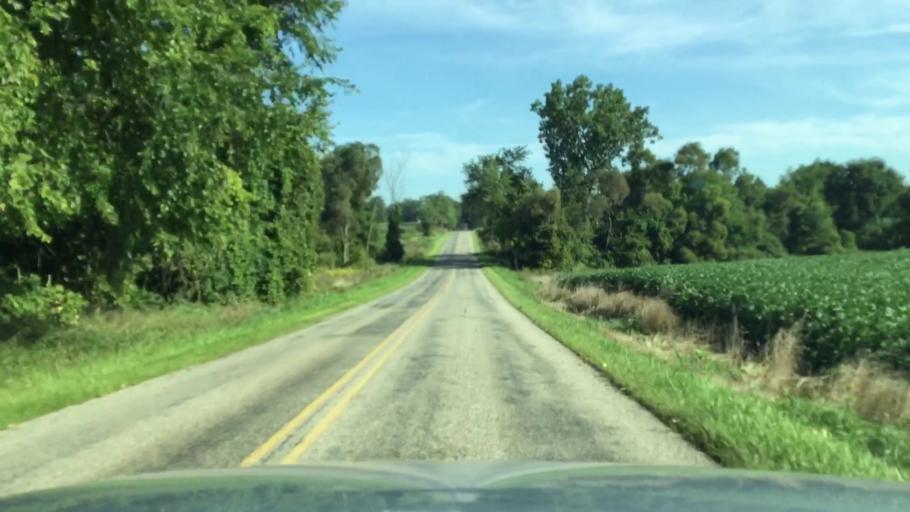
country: US
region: Michigan
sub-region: Lenawee County
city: Hudson
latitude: 41.9148
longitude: -84.4205
